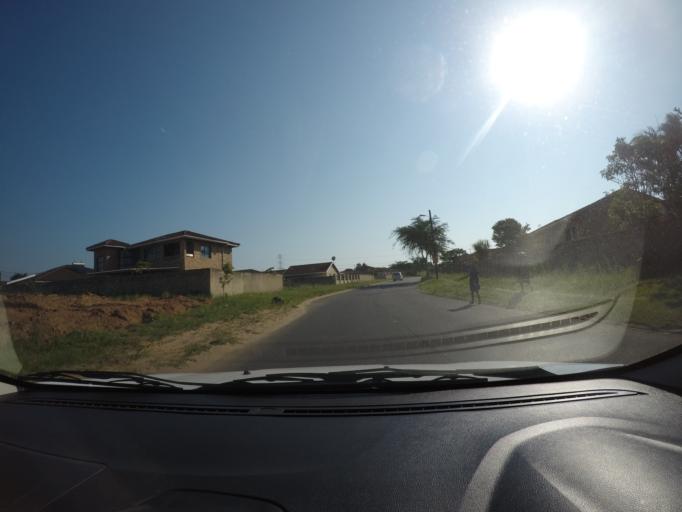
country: ZA
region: KwaZulu-Natal
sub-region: uThungulu District Municipality
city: Richards Bay
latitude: -28.7243
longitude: 32.0379
